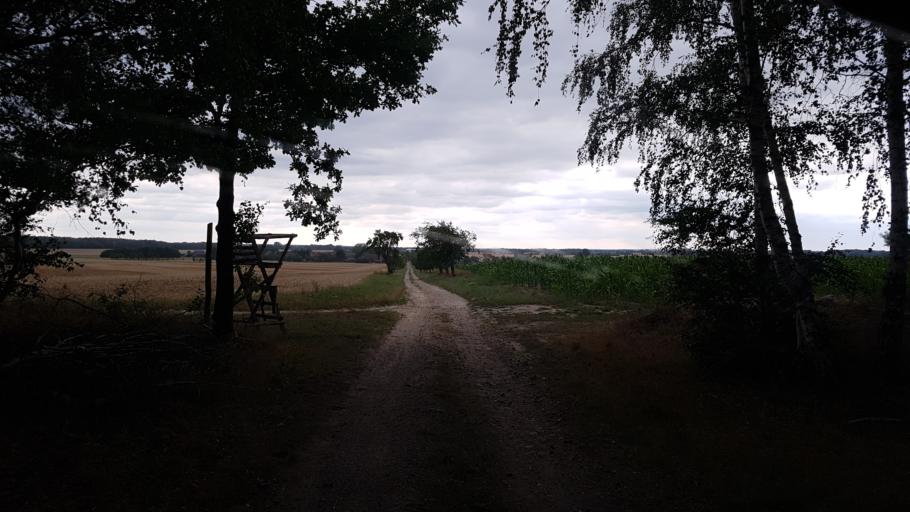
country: DE
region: Brandenburg
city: Sonnewalde
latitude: 51.7132
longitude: 13.7033
